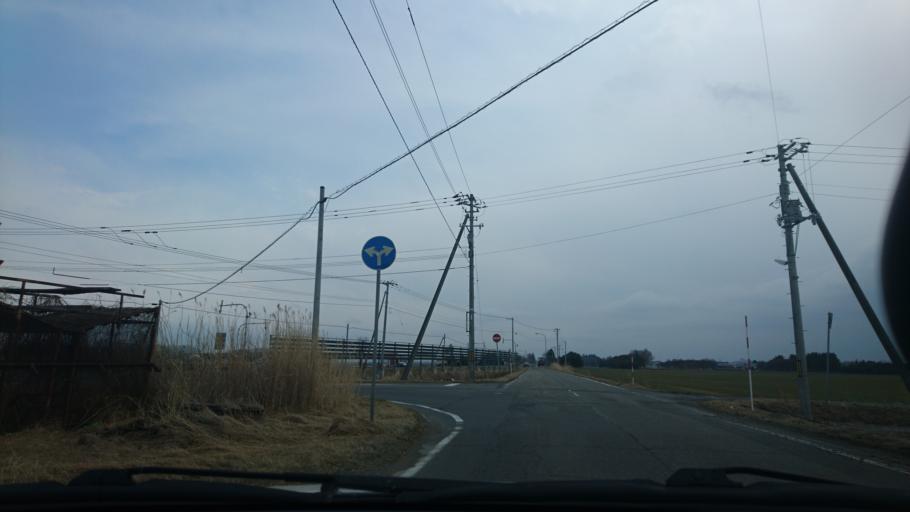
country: JP
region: Hokkaido
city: Otofuke
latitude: 43.0329
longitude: 143.2043
